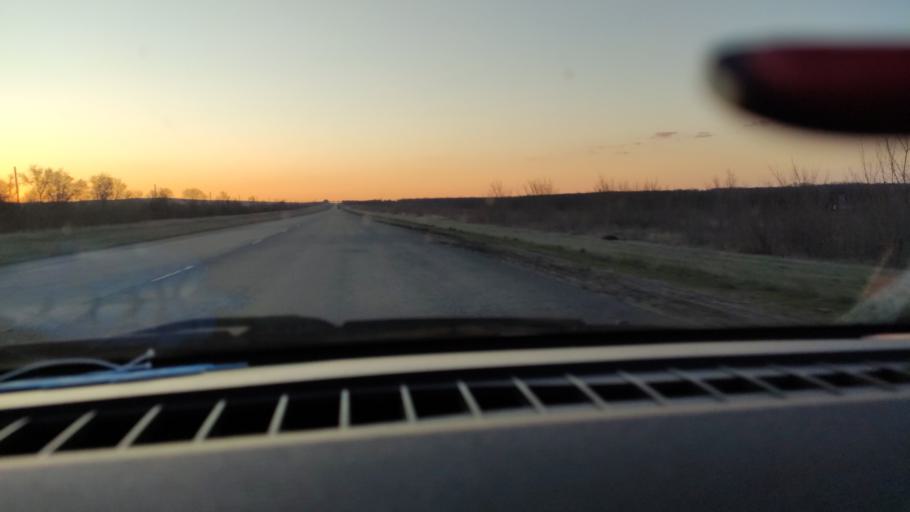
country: RU
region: Saratov
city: Yelshanka
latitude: 51.8296
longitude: 46.2464
